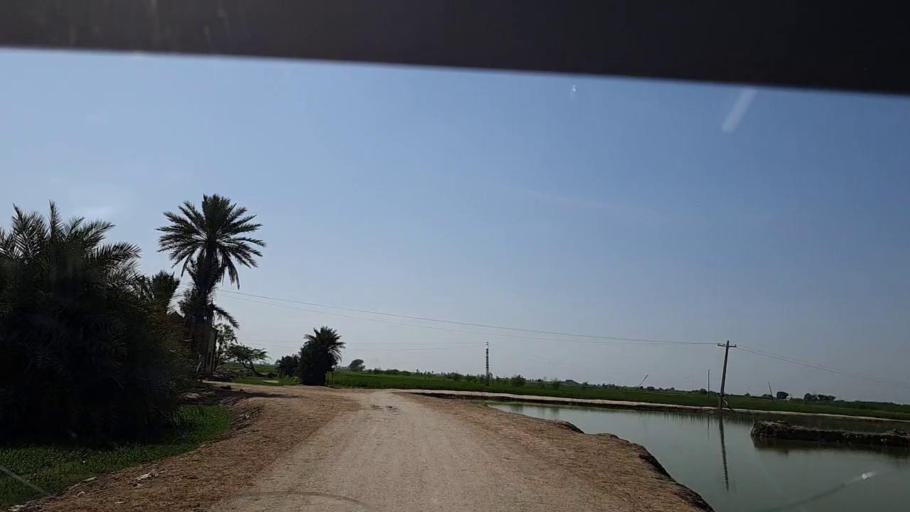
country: PK
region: Sindh
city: Tangwani
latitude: 28.3198
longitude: 69.0891
